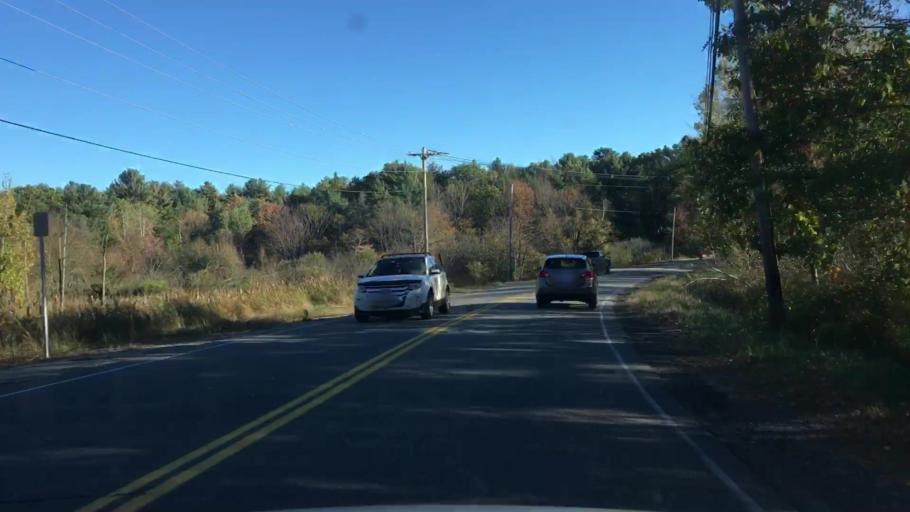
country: US
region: Maine
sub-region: Cumberland County
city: South Portland Gardens
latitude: 43.6154
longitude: -70.3419
